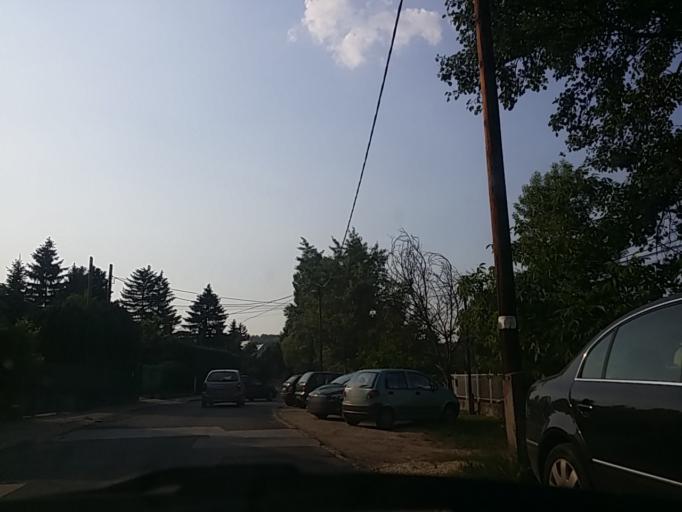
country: HU
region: Pest
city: Budakalasz
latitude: 47.5932
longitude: 19.0433
